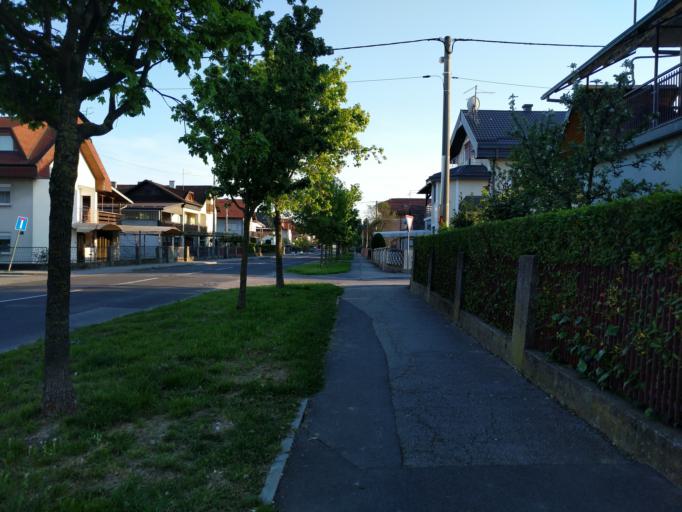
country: HR
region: Grad Zagreb
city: Dubrava
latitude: 45.8319
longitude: 16.0825
